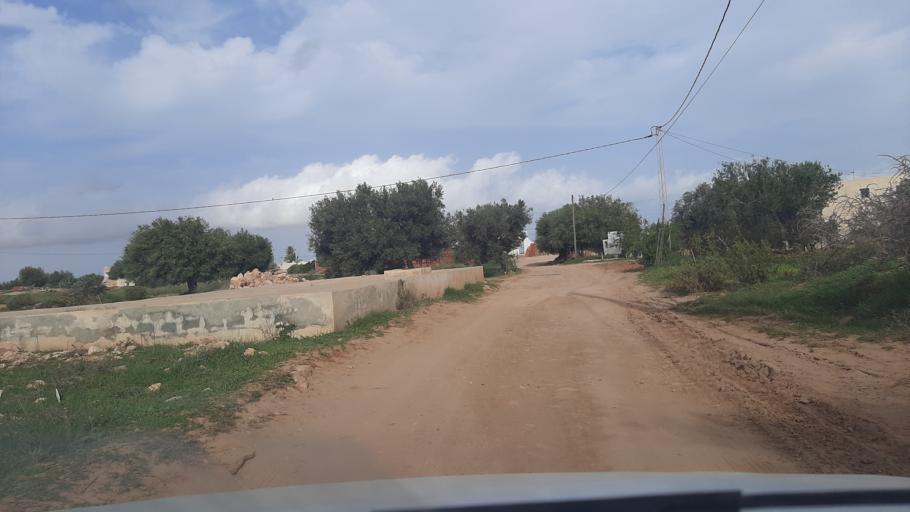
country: TN
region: Madanin
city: Midoun
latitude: 33.8060
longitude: 11.0242
